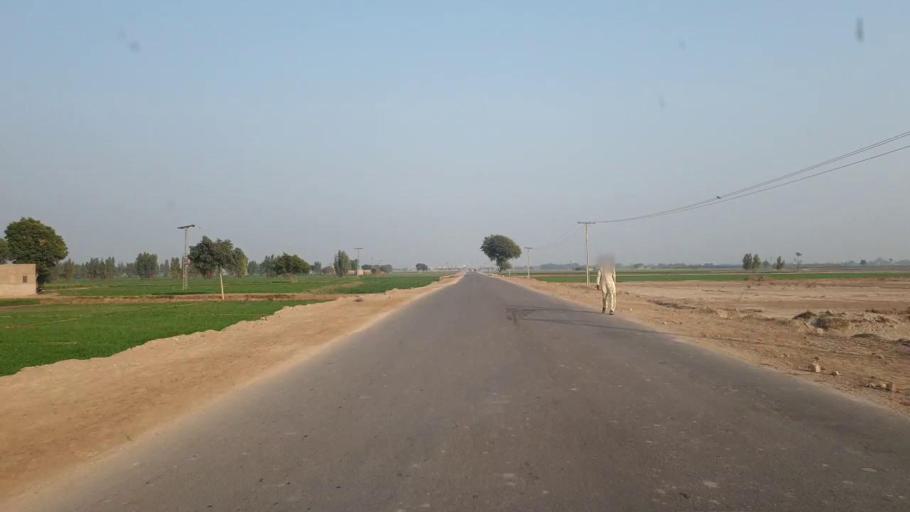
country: PK
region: Sindh
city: Bhit Shah
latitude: 25.8086
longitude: 68.4666
